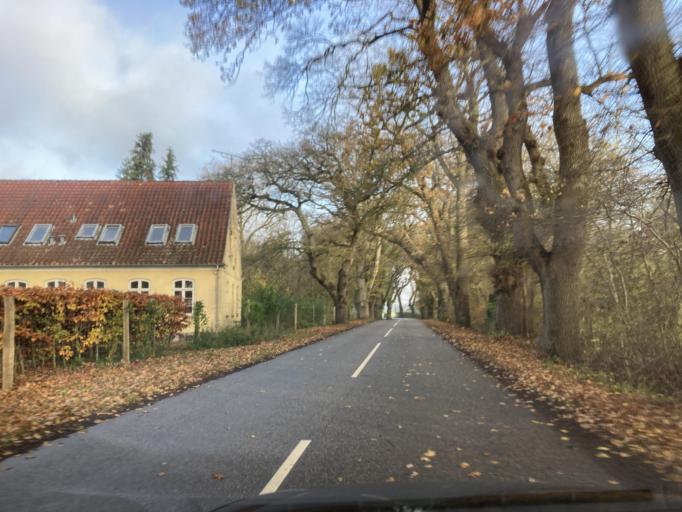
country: DK
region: Zealand
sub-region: Lolland Kommune
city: Rodby
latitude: 54.7565
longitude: 11.3547
